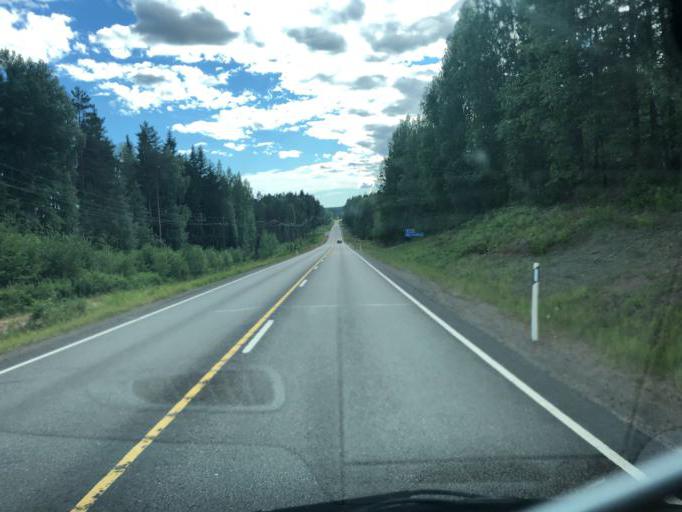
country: FI
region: Kymenlaakso
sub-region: Kouvola
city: Kouvola
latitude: 60.9725
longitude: 26.8991
